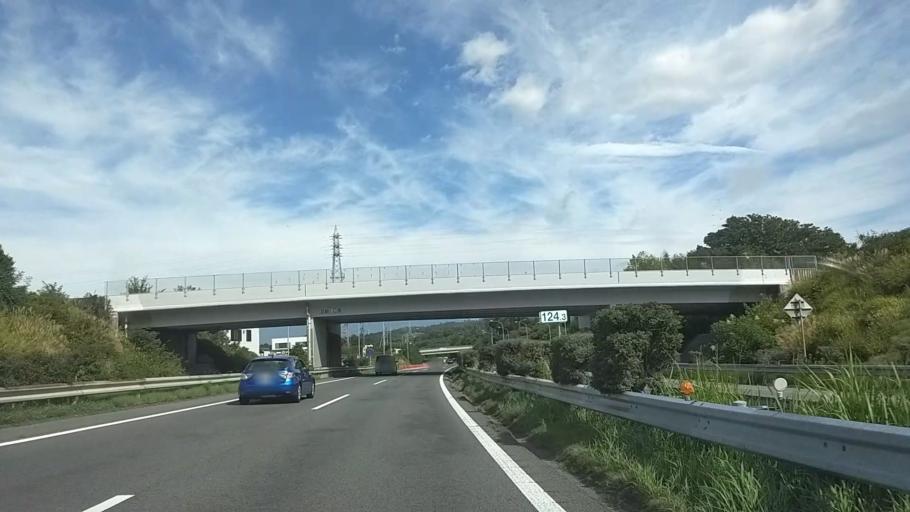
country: JP
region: Yamanashi
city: Nirasaki
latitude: 35.7192
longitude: 138.4654
